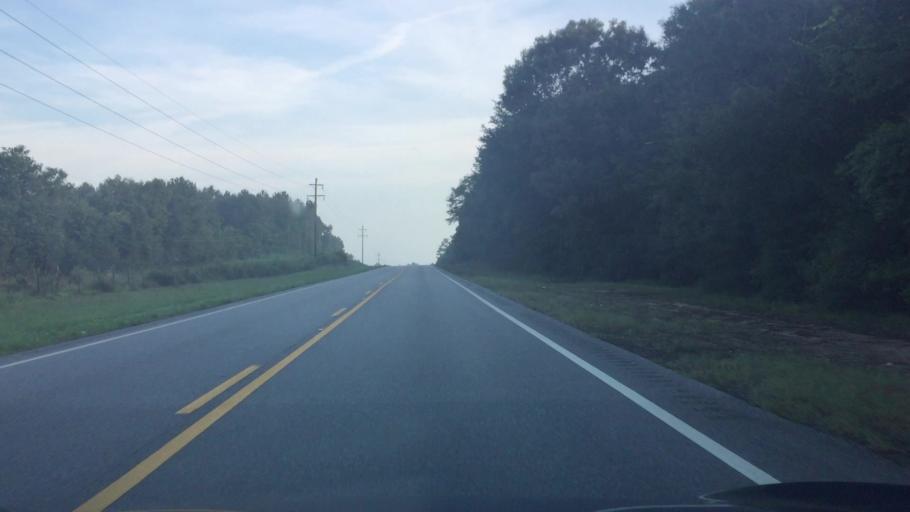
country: US
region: Alabama
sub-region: Covington County
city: Florala
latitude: 31.0674
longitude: -86.4010
